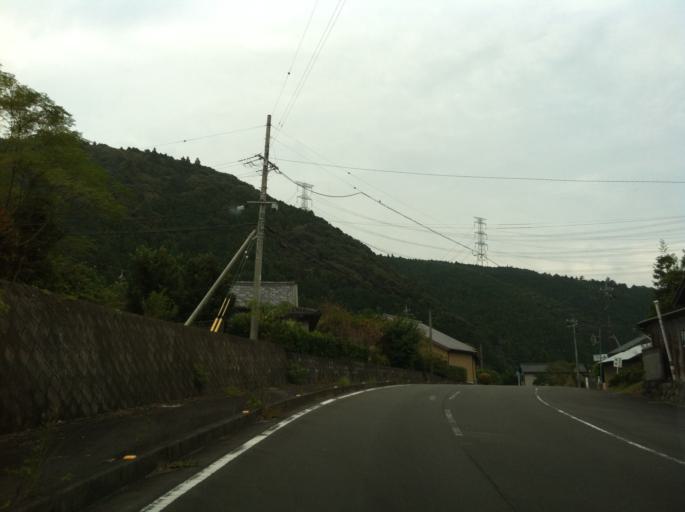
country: JP
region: Shizuoka
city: Mori
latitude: 34.8658
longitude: 138.0180
